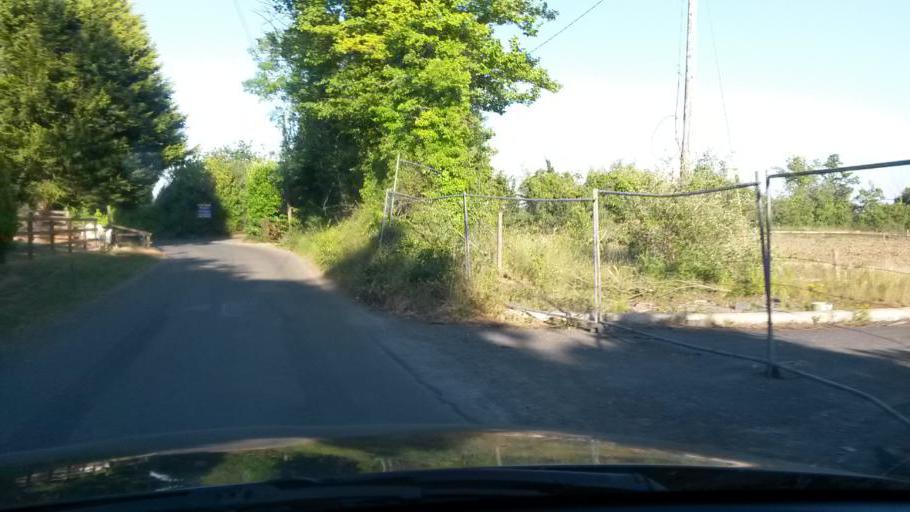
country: IE
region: Leinster
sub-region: Fingal County
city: Swords
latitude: 53.4905
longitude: -6.2927
